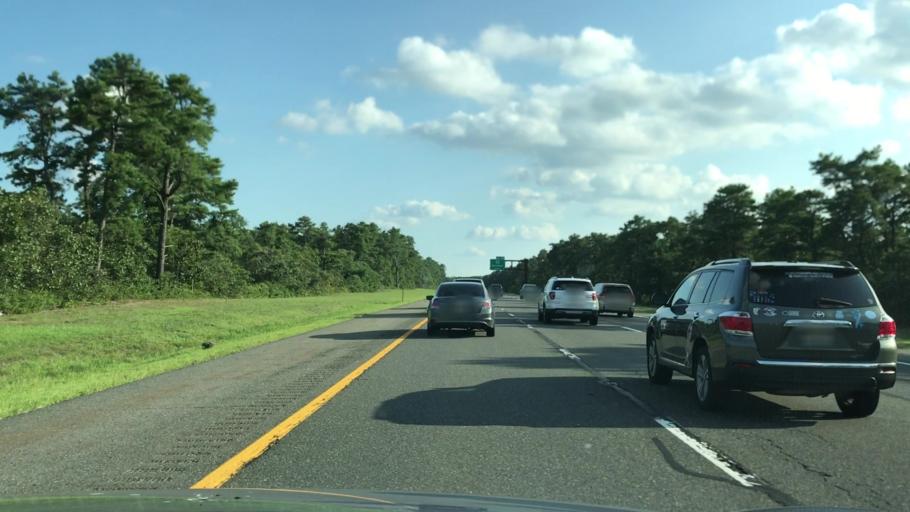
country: US
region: New Jersey
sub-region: Ocean County
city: Waretown
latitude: 39.8105
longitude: -74.2319
